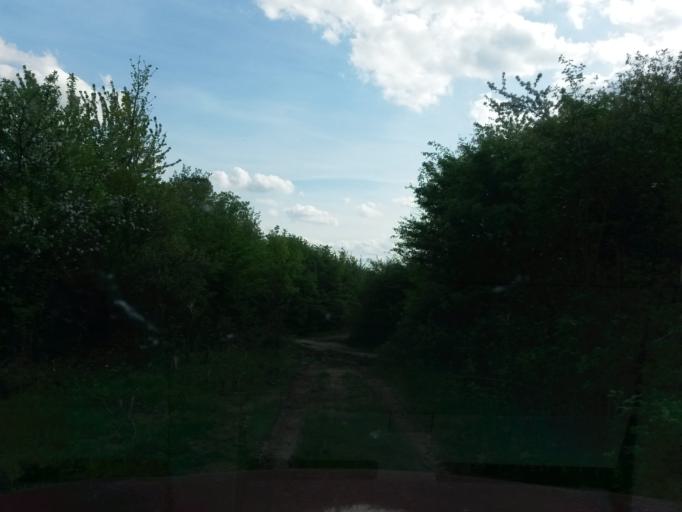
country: SK
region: Kosicky
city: Kosice
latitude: 48.7233
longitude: 21.2123
